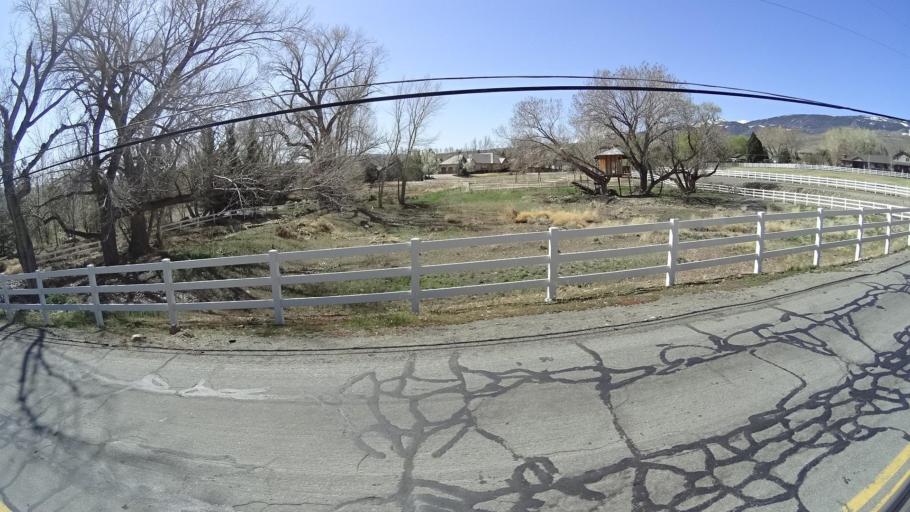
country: US
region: Nevada
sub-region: Washoe County
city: Reno
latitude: 39.4547
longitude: -119.8075
